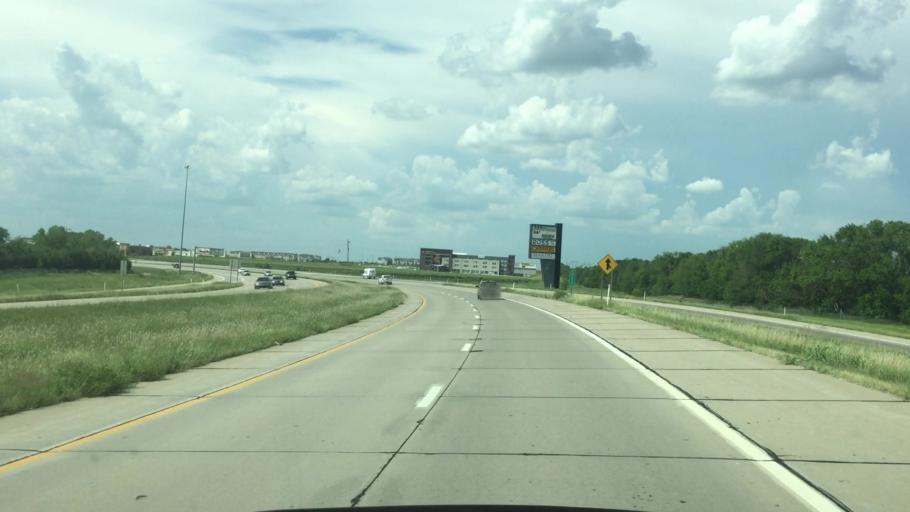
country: US
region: Kansas
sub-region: Butler County
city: Andover
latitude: 37.7245
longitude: -97.1993
